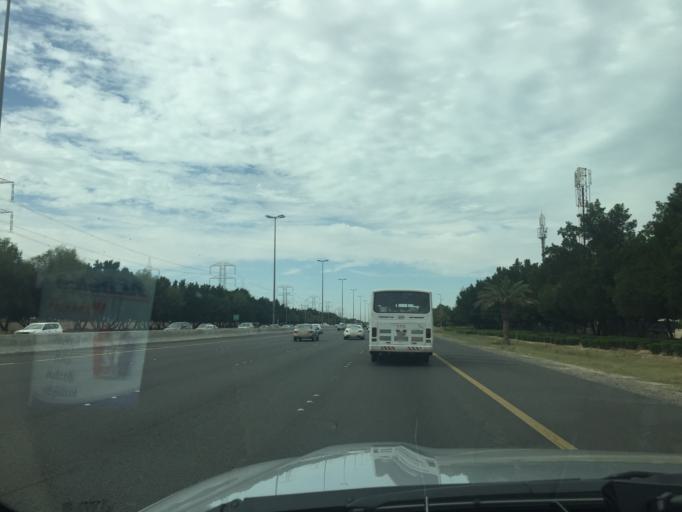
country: KW
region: Mubarak al Kabir
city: Sabah as Salim
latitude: 29.2468
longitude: 48.0480
